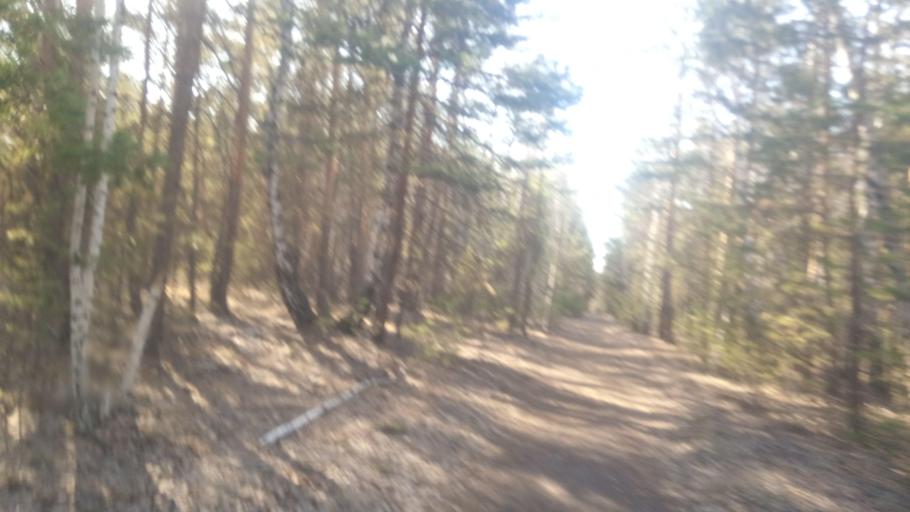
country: RU
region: Chelyabinsk
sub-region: Gorod Chelyabinsk
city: Chelyabinsk
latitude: 55.1594
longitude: 61.3376
